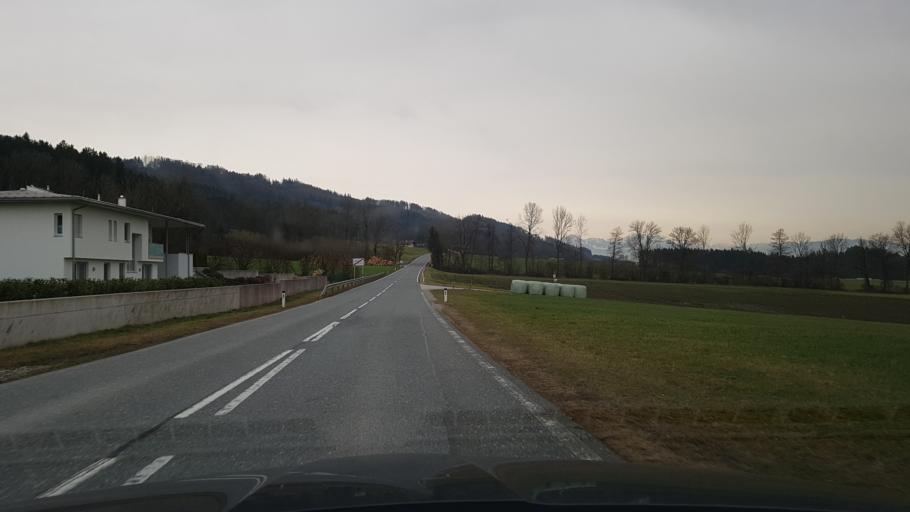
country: AT
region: Salzburg
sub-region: Politischer Bezirk Salzburg-Umgebung
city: Nussdorf am Haunsberg
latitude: 47.9477
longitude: 13.0017
